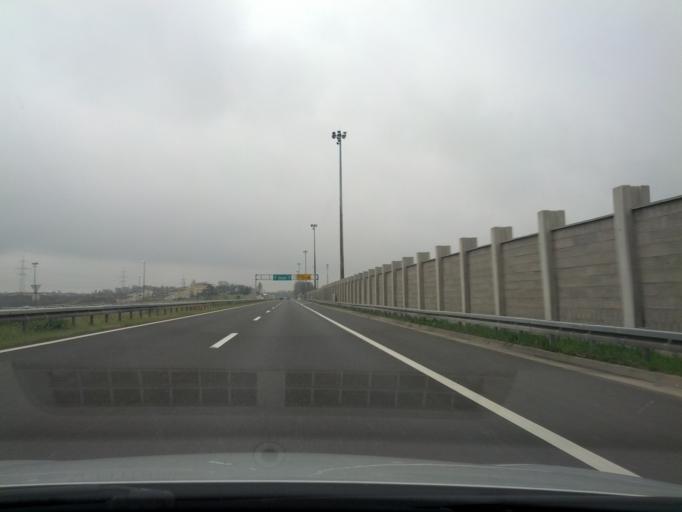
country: HR
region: Zagrebacka
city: Bestovje
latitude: 45.8001
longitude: 15.7818
